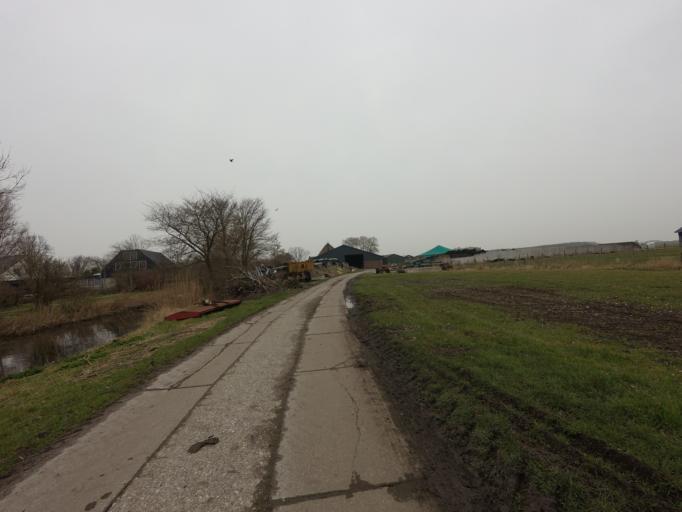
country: NL
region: Friesland
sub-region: Gemeente Franekeradeel
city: Franeker
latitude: 53.1930
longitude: 5.5551
